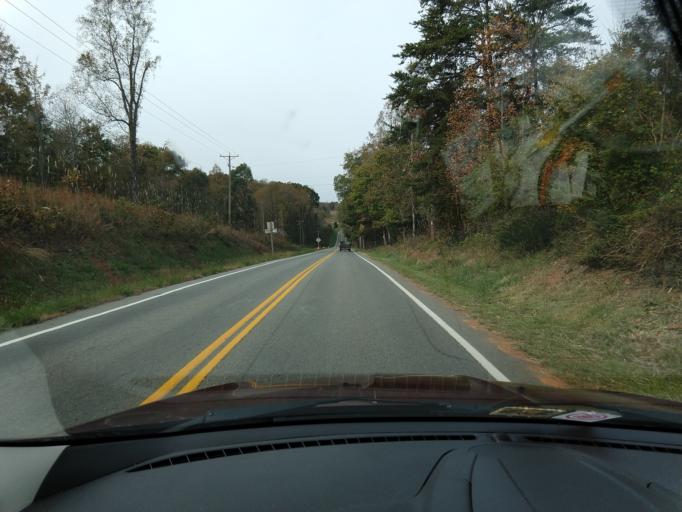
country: US
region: Virginia
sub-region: Franklin County
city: Union Hall
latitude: 36.9880
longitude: -79.6551
